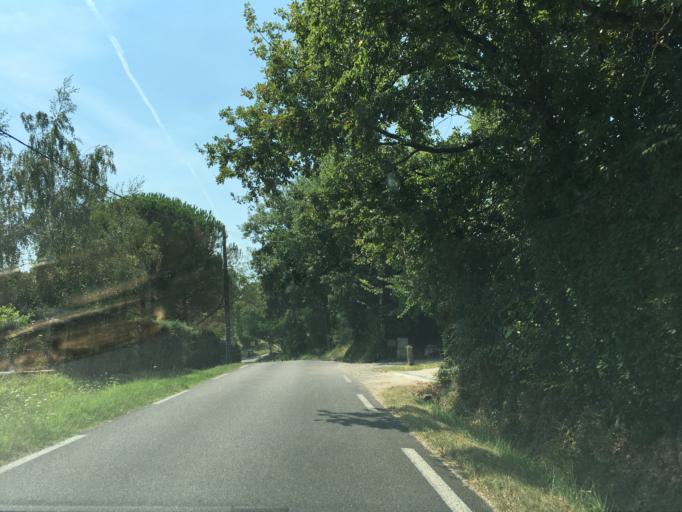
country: FR
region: Midi-Pyrenees
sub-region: Departement du Tarn-et-Garonne
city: Saint-Nauphary
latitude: 43.9672
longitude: 1.3930
